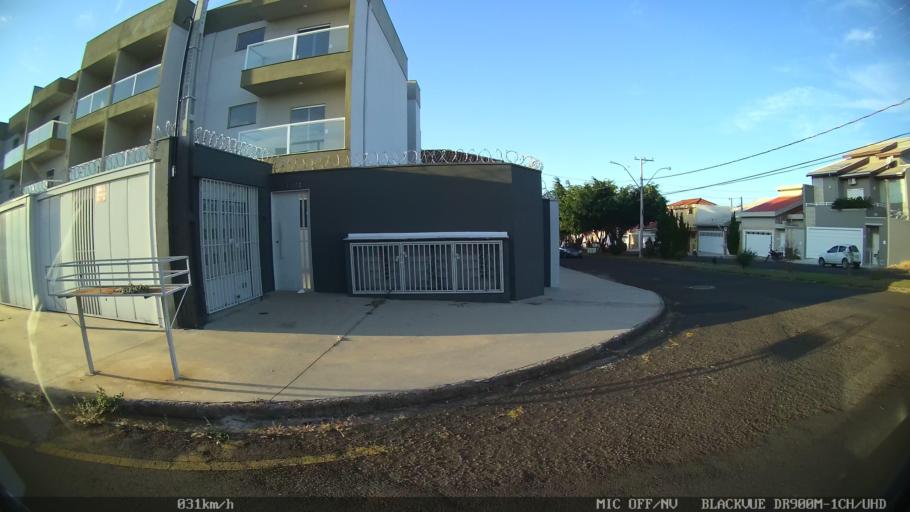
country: BR
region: Sao Paulo
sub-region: Franca
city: Franca
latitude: -20.5058
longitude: -47.3901
